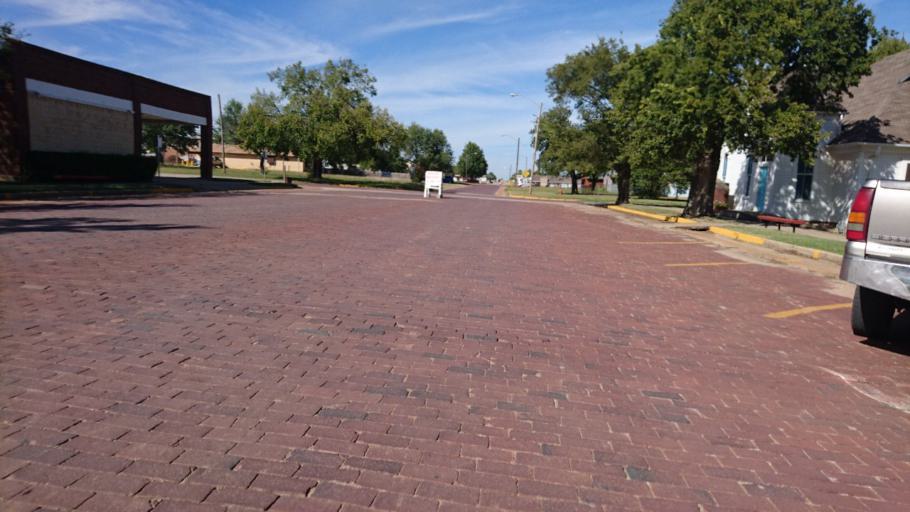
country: US
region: Oklahoma
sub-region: Lincoln County
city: Stroud
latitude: 35.7065
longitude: -96.7652
